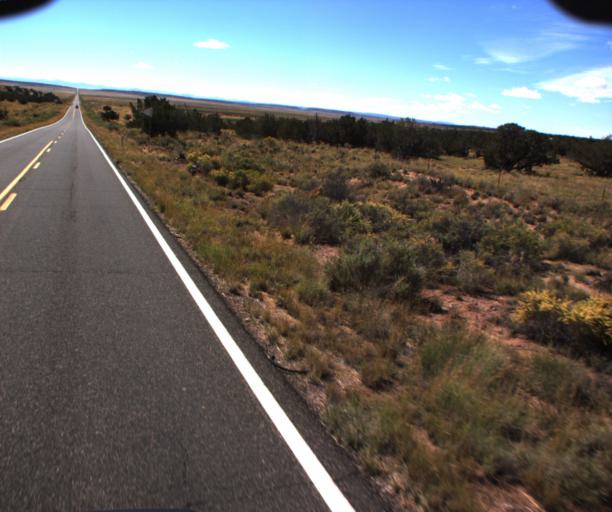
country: US
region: Arizona
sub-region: Apache County
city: Saint Johns
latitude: 34.7263
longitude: -109.2566
